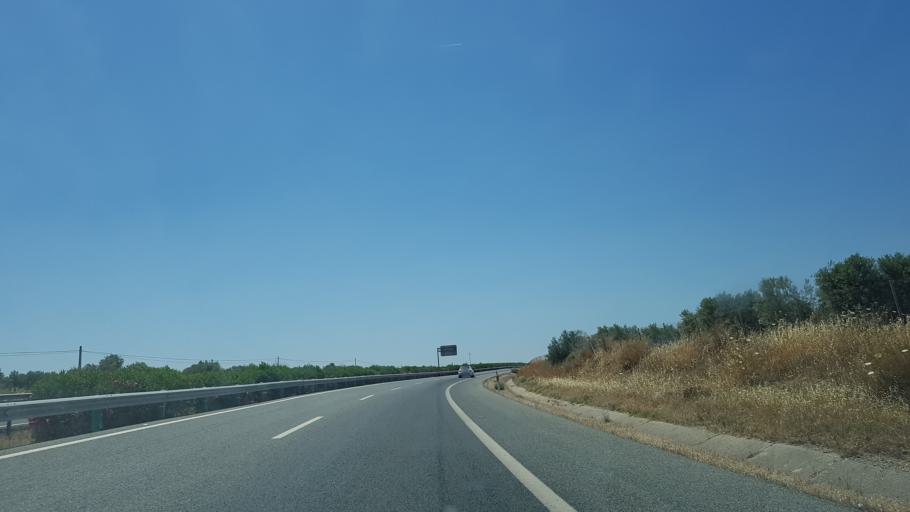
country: ES
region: Andalusia
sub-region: Provincia de Sevilla
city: La Puebla de Cazalla
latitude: 37.2267
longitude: -5.3353
